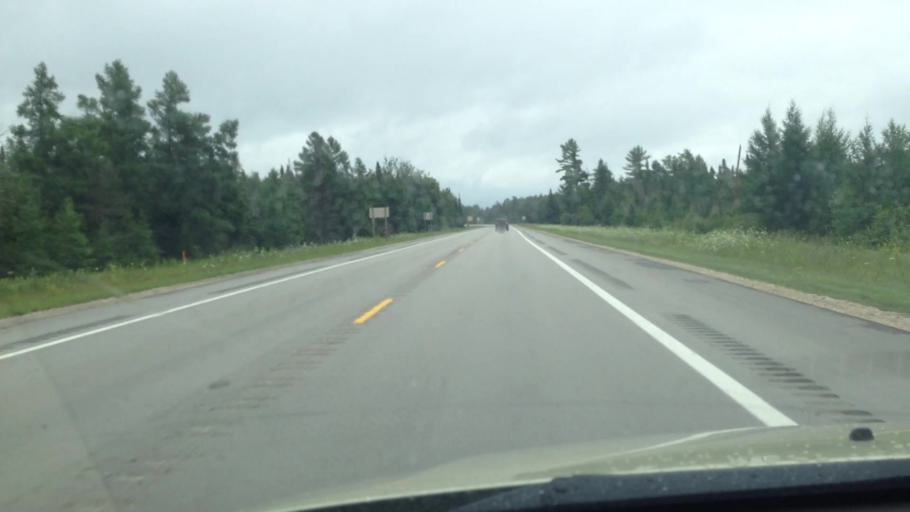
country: US
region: Michigan
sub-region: Schoolcraft County
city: Manistique
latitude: 45.8901
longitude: -86.5321
